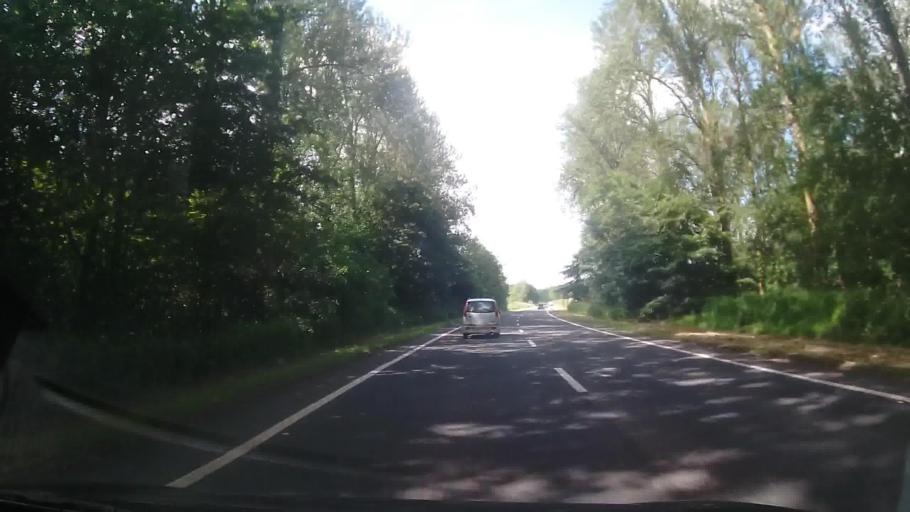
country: GB
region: England
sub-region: Herefordshire
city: Hope under Dinmore
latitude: 52.1822
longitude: -2.7160
